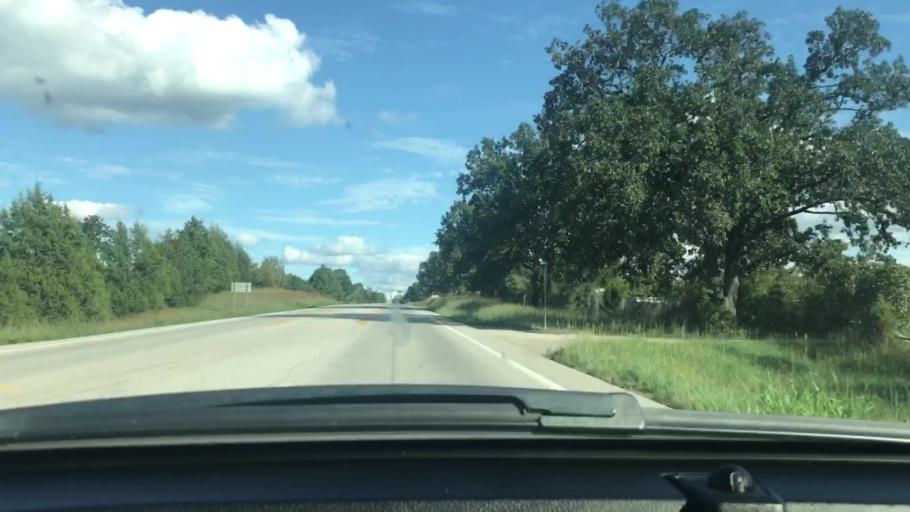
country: US
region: Missouri
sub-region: Howell County
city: West Plains
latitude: 36.6544
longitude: -91.6960
